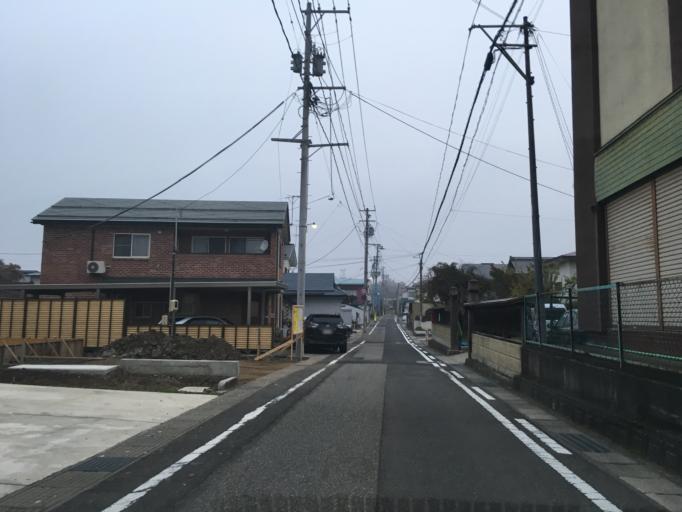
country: JP
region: Fukushima
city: Kitakata
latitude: 37.5009
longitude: 139.9383
